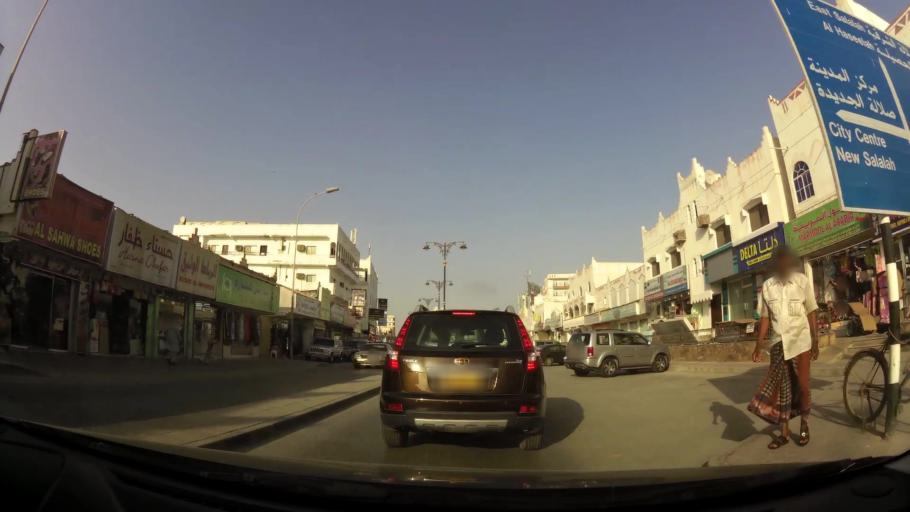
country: OM
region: Zufar
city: Salalah
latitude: 17.0126
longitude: 54.0925
